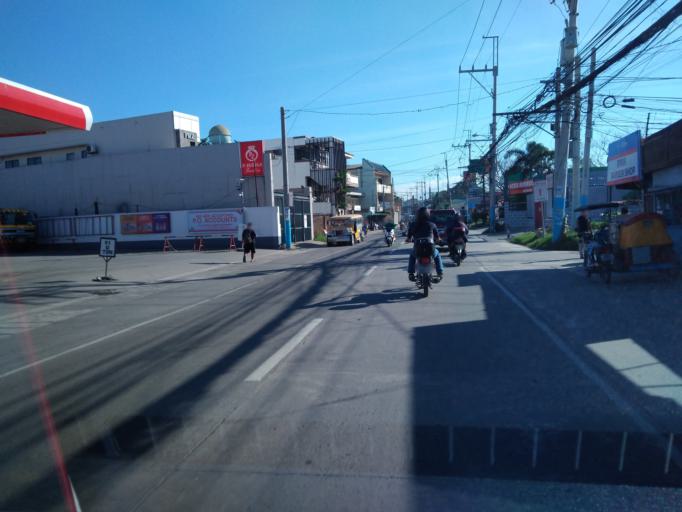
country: PH
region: Central Luzon
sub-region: Province of Bulacan
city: Meycauayan
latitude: 14.7383
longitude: 120.9647
